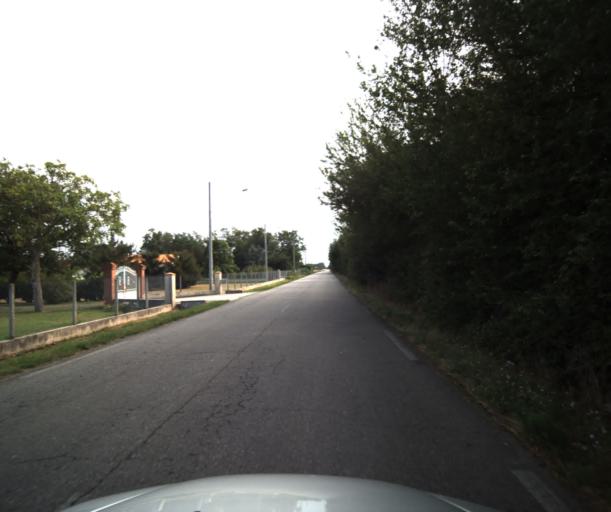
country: FR
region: Midi-Pyrenees
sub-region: Departement de la Haute-Garonne
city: Le Fauga
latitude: 43.4265
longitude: 1.3051
